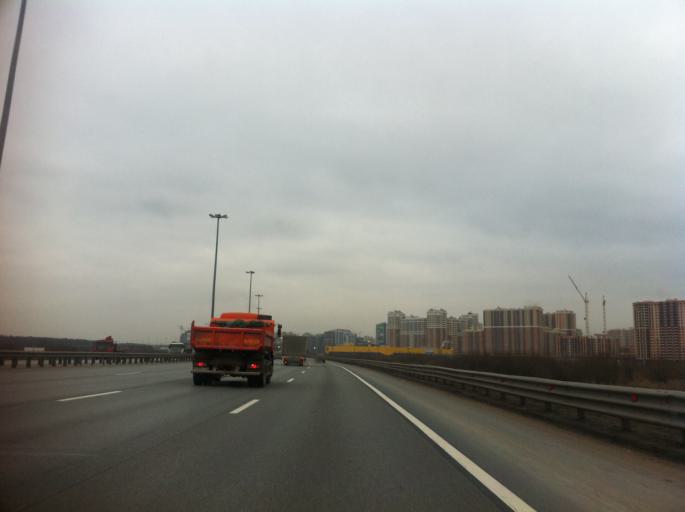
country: RU
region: St.-Petersburg
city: Krasnogvargeisky
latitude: 59.9234
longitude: 30.5282
